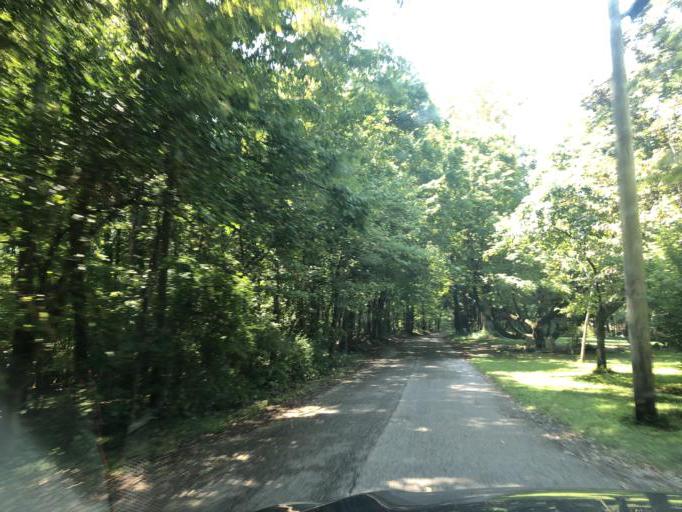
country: US
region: Tennessee
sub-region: Franklin County
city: Sewanee
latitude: 35.2038
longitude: -85.9305
